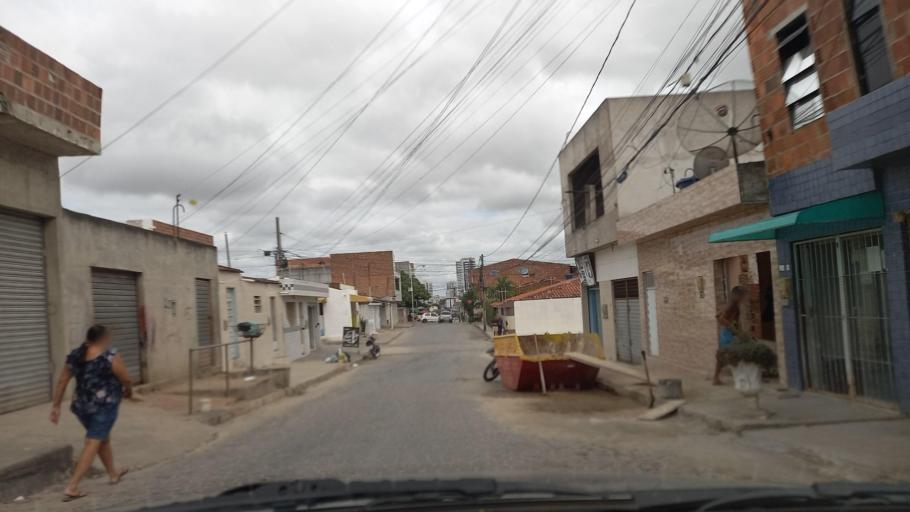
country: BR
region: Pernambuco
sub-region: Caruaru
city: Caruaru
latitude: -8.2704
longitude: -35.9557
